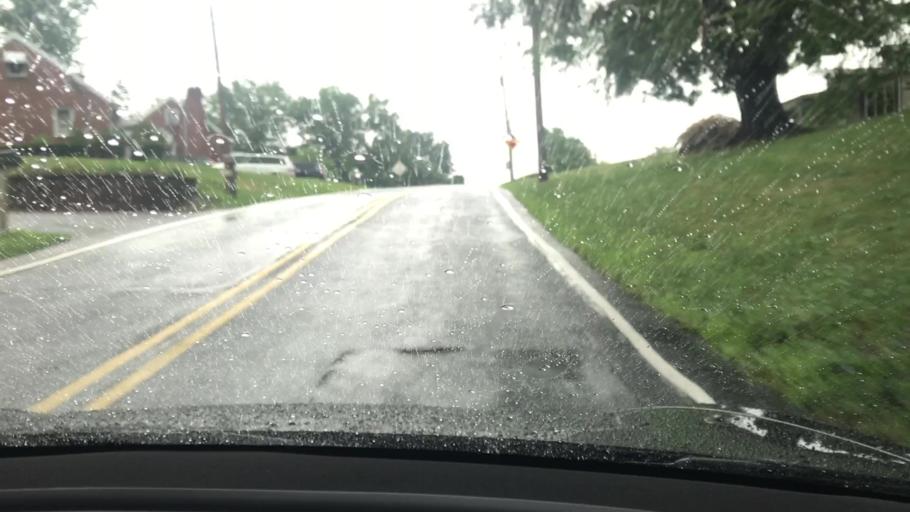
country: US
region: Pennsylvania
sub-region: Dauphin County
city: Paxtonia
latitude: 40.3216
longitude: -76.7988
